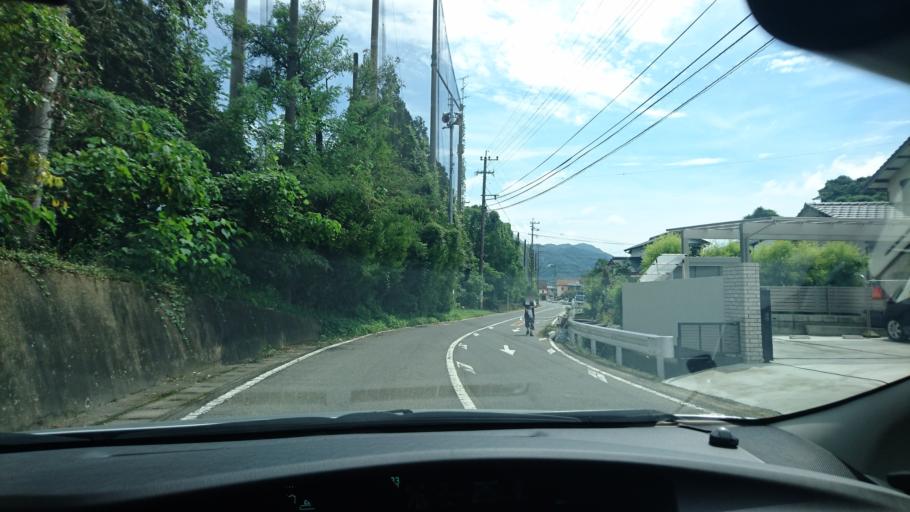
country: JP
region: Saga Prefecture
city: Takeocho-takeo
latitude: 33.2227
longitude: 130.0722
